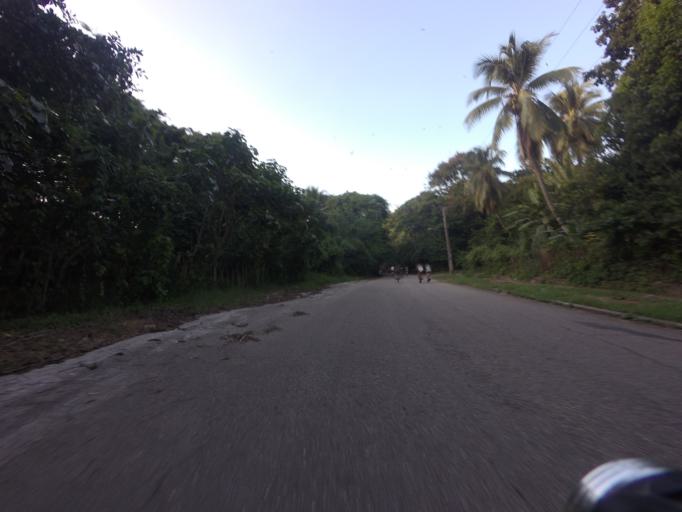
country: CU
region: La Habana
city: Cerro
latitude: 23.1111
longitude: -82.4051
